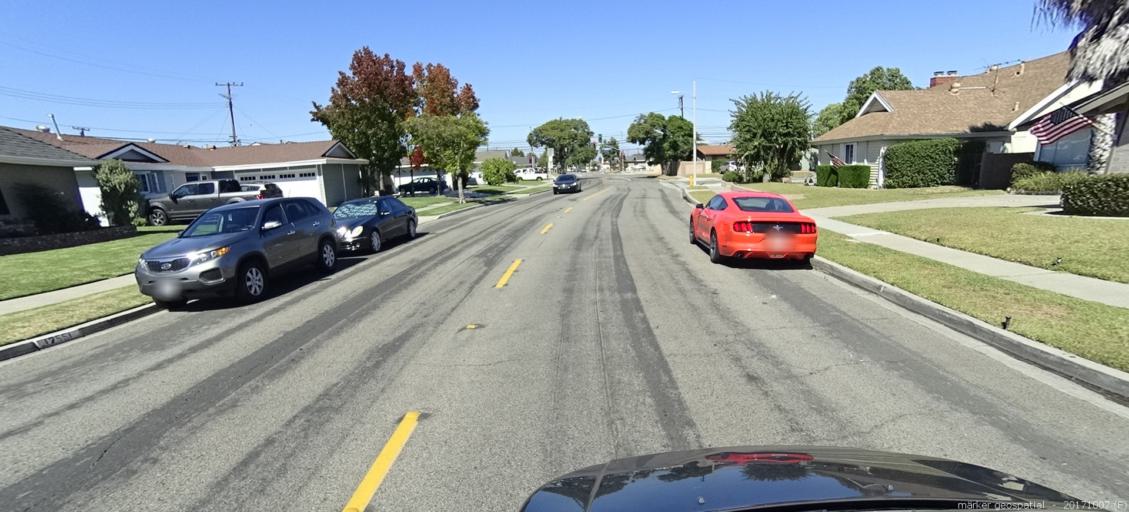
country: US
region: California
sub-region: Orange County
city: Westminster
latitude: 33.7802
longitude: -118.0239
